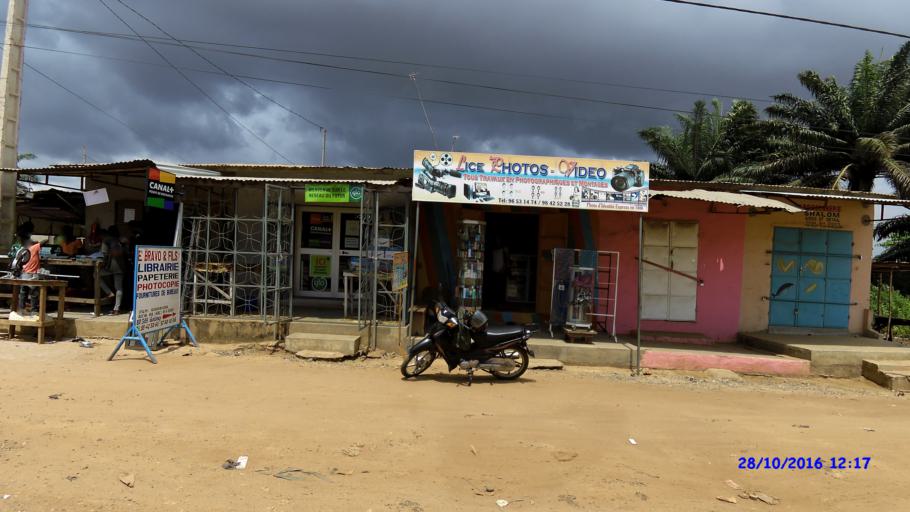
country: BJ
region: Atlantique
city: Hevie
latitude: 6.3874
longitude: 2.2963
